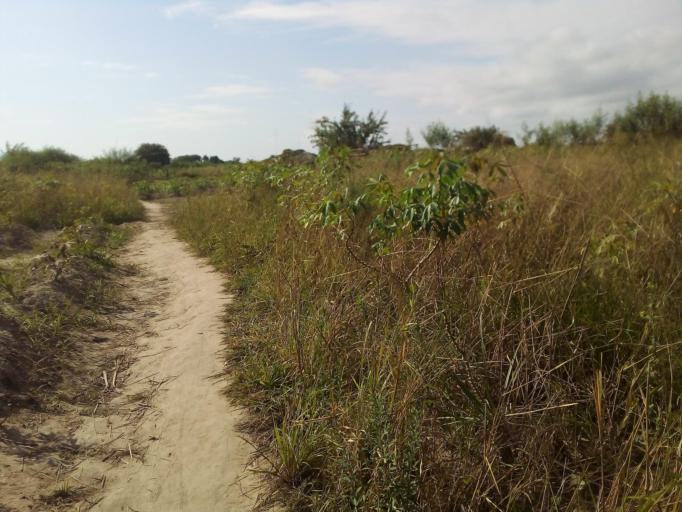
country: MZ
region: Zambezia
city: Quelimane
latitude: -17.5515
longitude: 36.7080
